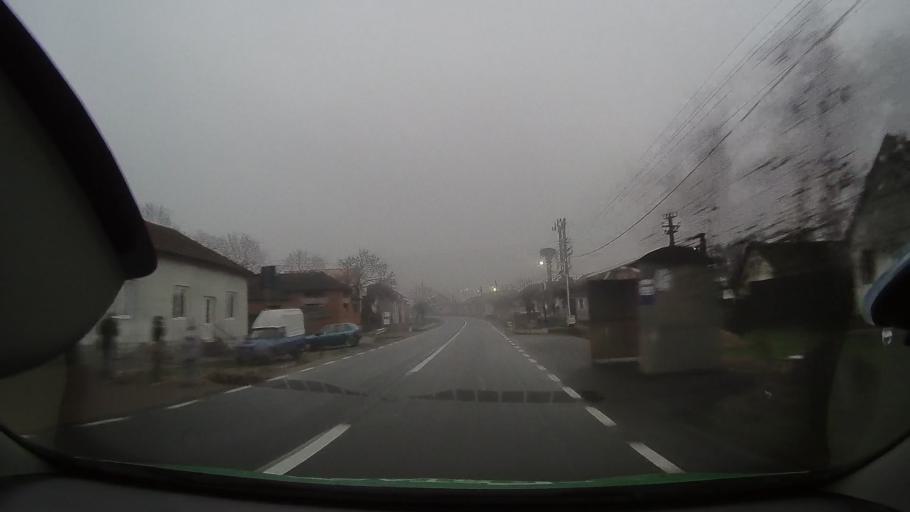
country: RO
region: Bihor
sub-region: Comuna Olcea
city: Calacea
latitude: 46.6373
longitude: 21.9560
